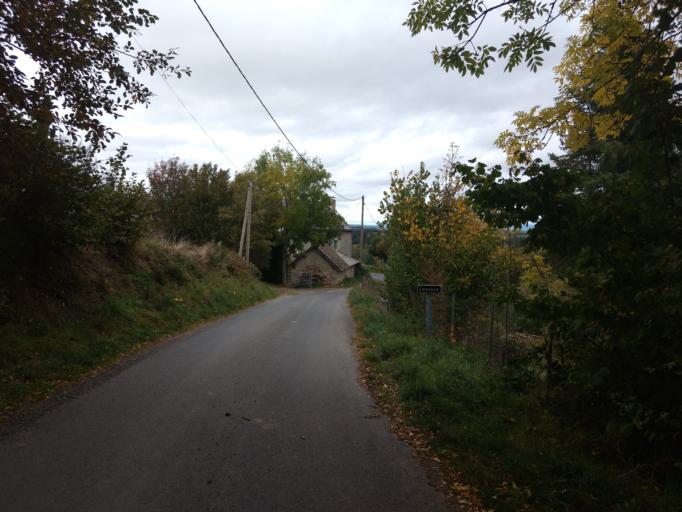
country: FR
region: Auvergne
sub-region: Departement du Cantal
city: Chaudes-Aigues
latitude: 44.8385
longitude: 3.0018
